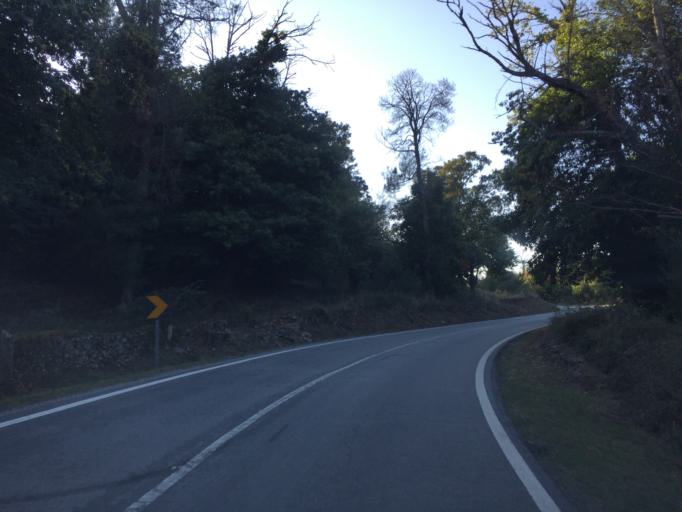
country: PT
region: Portalegre
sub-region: Castelo de Vide
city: Castelo de Vide
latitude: 39.4006
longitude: -7.4321
